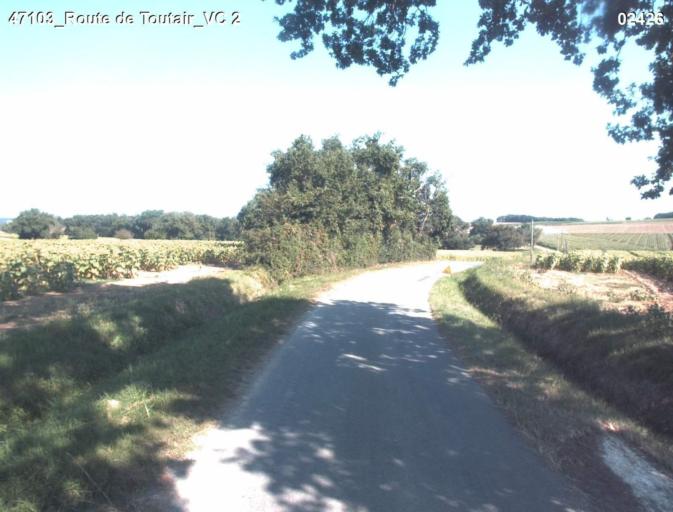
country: FR
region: Aquitaine
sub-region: Departement du Lot-et-Garonne
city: Nerac
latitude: 44.0675
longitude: 0.3336
